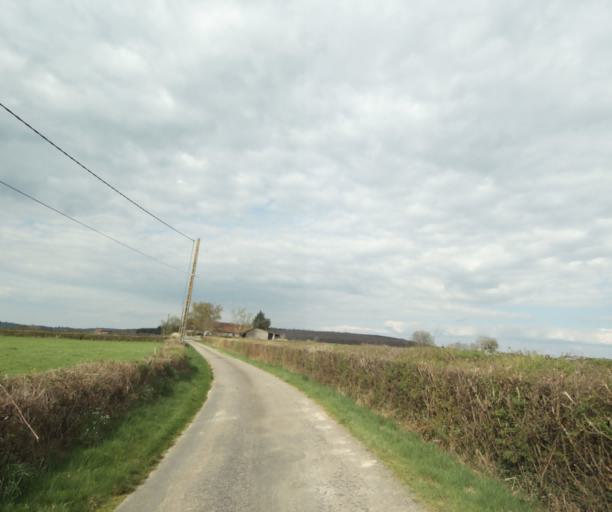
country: FR
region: Bourgogne
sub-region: Departement de Saone-et-Loire
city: Saint-Vallier
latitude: 46.5428
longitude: 4.3998
